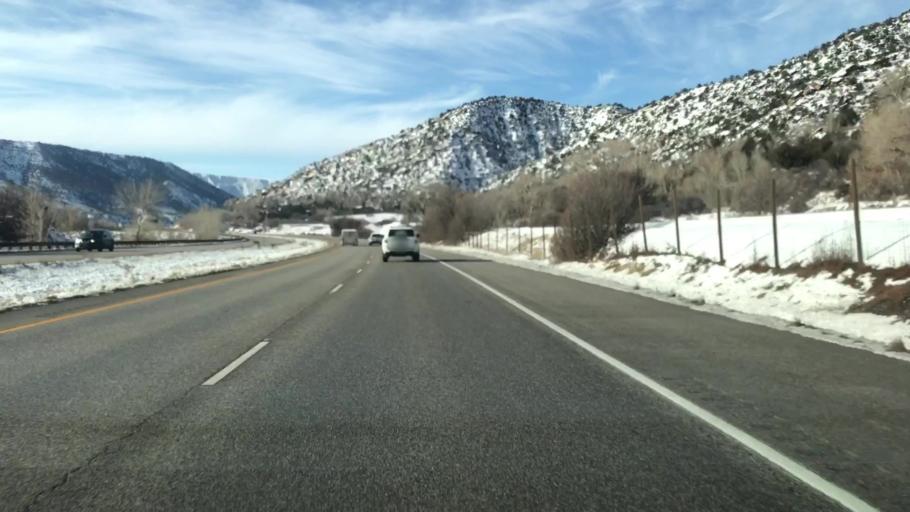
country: US
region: Colorado
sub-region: Garfield County
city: New Castle
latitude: 39.5675
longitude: -107.5473
